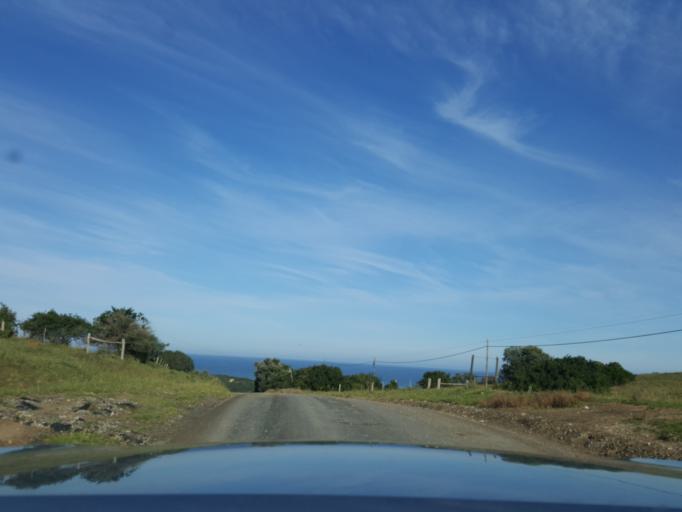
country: ZA
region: Eastern Cape
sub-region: Cacadu District Municipality
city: Port Alfred
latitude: -33.6434
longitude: 26.7342
